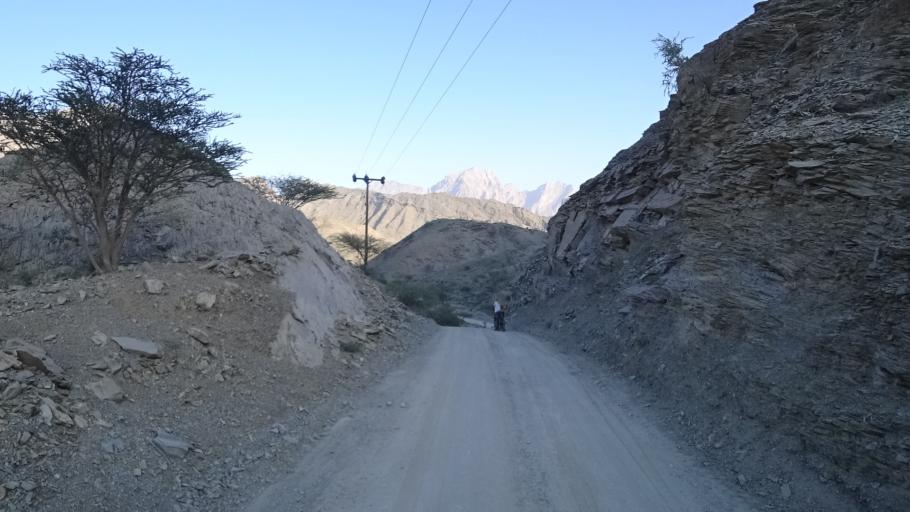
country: OM
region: Al Batinah
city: Rustaq
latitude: 23.2720
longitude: 57.3839
